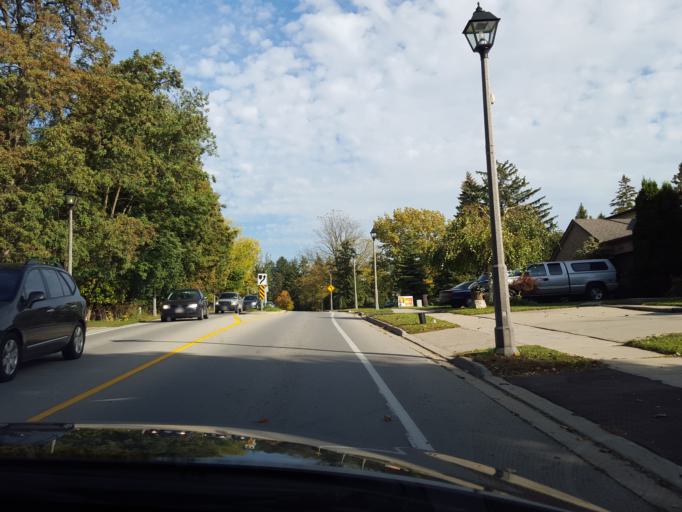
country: CA
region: Ontario
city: Ancaster
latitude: 43.2290
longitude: -79.9679
